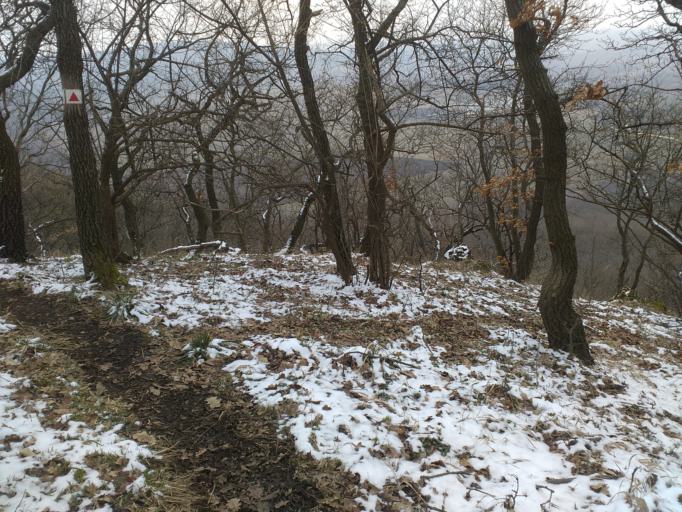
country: HU
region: Komarom-Esztergom
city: Piliscsev
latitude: 47.6849
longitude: 18.8419
